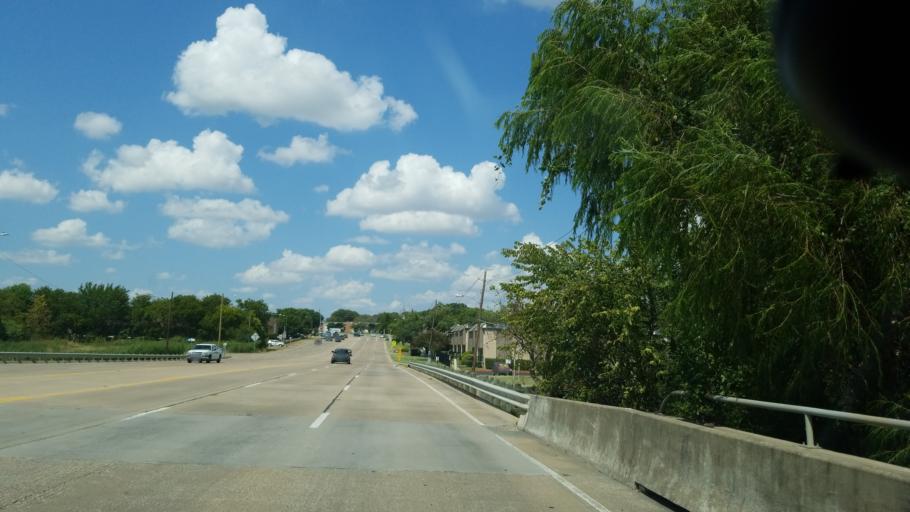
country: US
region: Texas
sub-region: Dallas County
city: Grand Prairie
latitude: 32.7321
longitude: -96.9941
